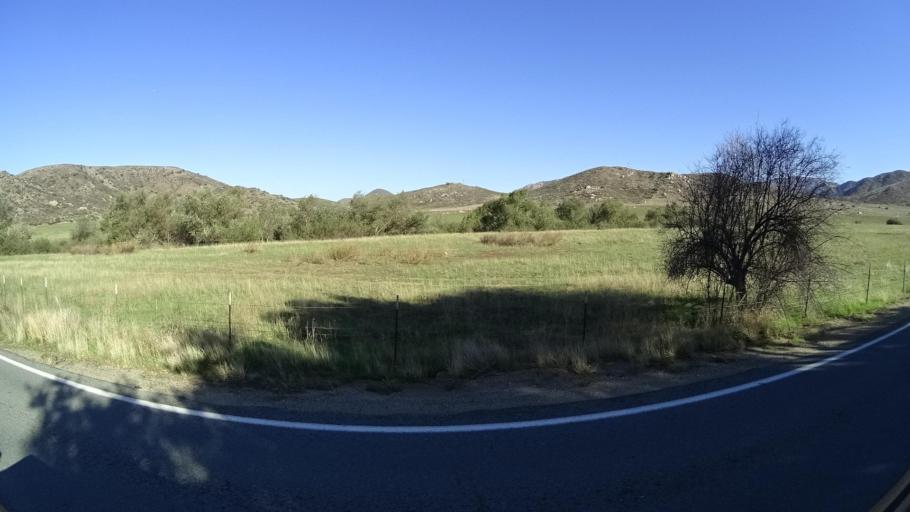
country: US
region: California
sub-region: San Diego County
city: Jamul
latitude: 32.6672
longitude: -116.8315
